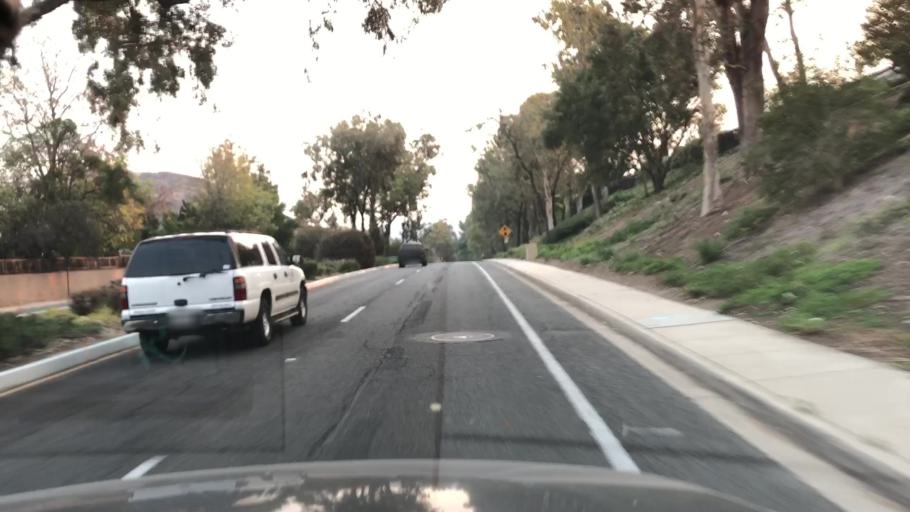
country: US
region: California
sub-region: Ventura County
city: Casa Conejo
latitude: 34.2019
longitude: -118.8903
